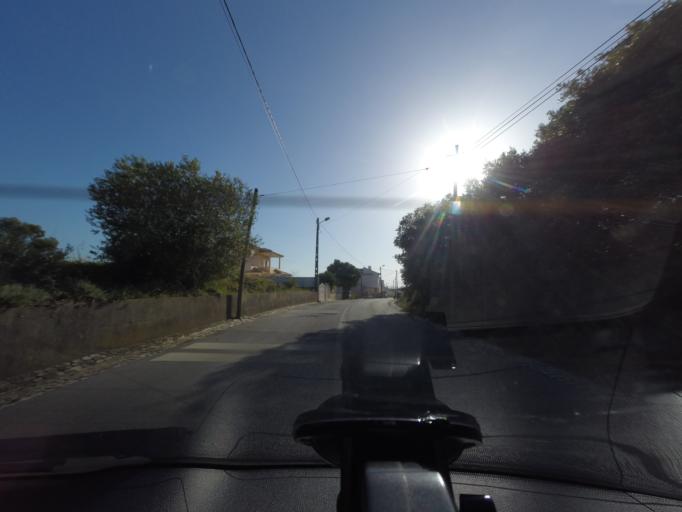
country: PT
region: Lisbon
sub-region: Cascais
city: Alcabideche
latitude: 38.7448
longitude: -9.4323
